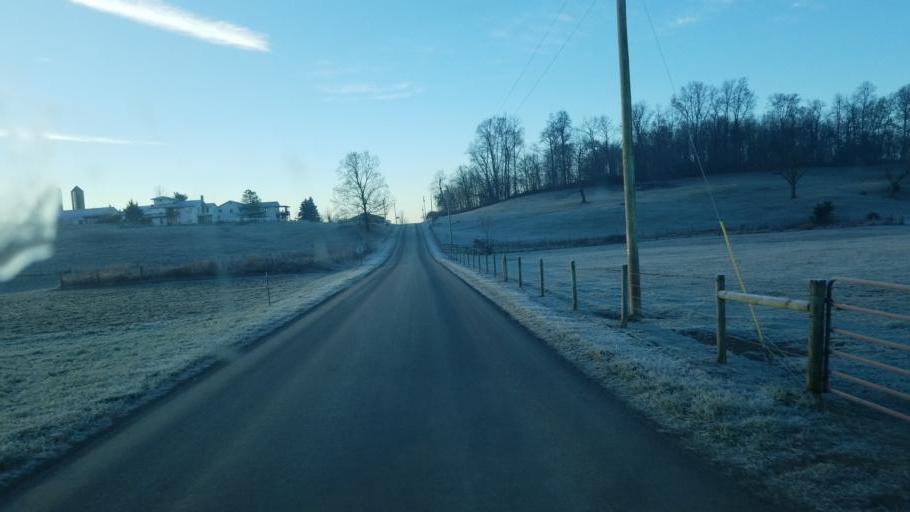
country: US
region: Ohio
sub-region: Holmes County
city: Millersburg
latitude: 40.5983
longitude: -81.8008
